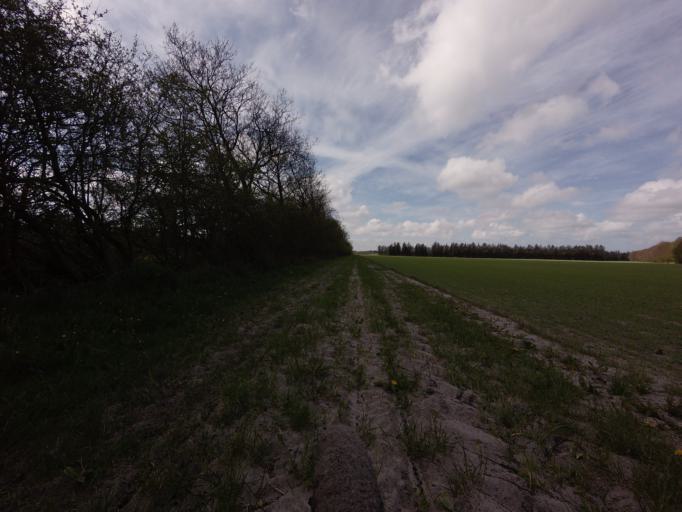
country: DK
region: North Denmark
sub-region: Jammerbugt Kommune
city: Kas
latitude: 57.1975
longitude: 9.6204
